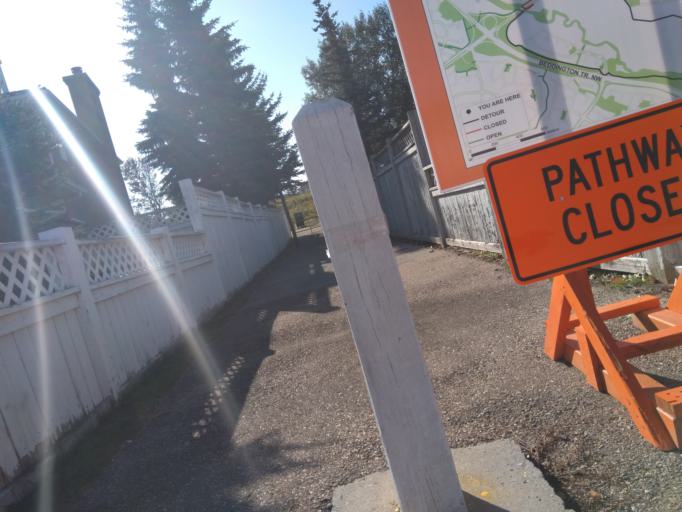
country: CA
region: Alberta
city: Calgary
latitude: 51.1425
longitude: -114.0889
